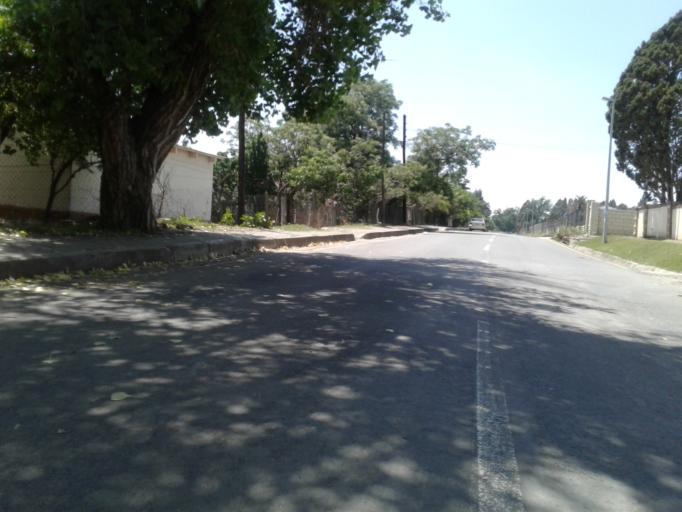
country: LS
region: Maseru
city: Maseru
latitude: -29.3038
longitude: 27.4750
